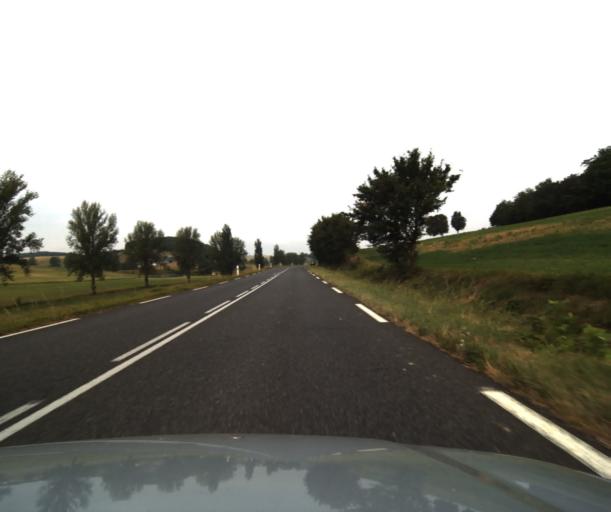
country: FR
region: Midi-Pyrenees
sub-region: Departement du Gers
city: Pavie
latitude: 43.5627
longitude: 0.5102
